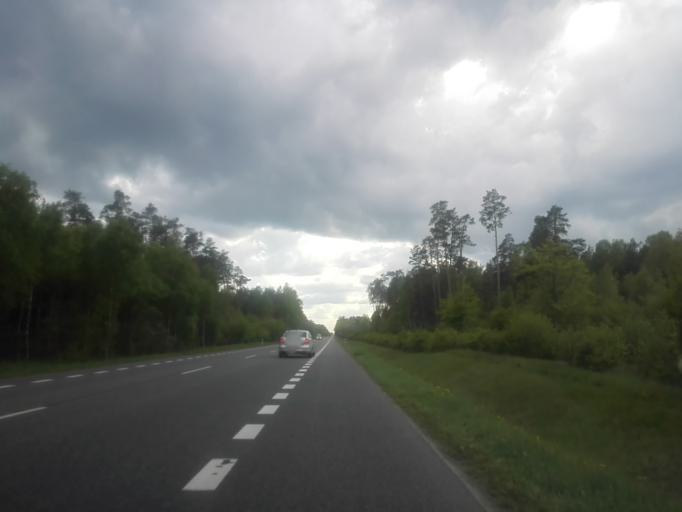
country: PL
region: Masovian Voivodeship
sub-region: Powiat ostrowski
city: Ostrow Mazowiecka
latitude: 52.8445
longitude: 21.9704
